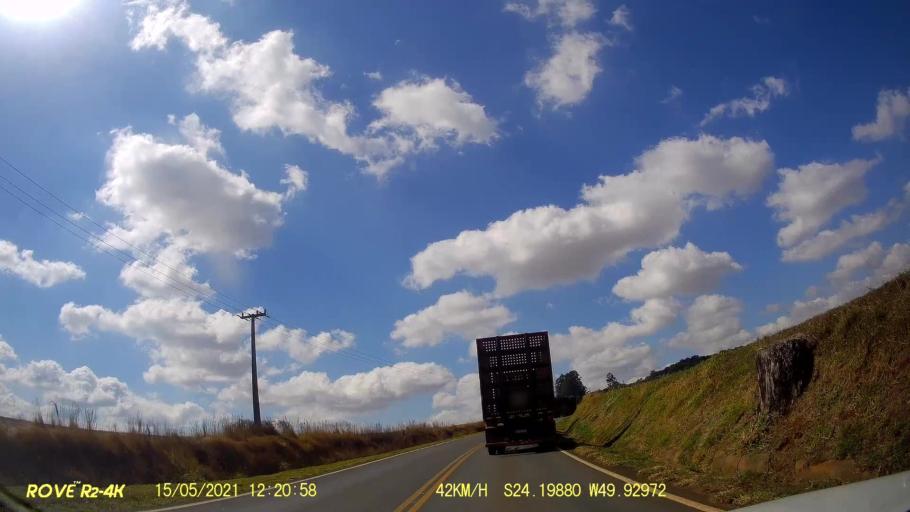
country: BR
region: Parana
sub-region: Jaguariaiva
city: Jaguariaiva
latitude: -24.1988
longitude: -49.9297
